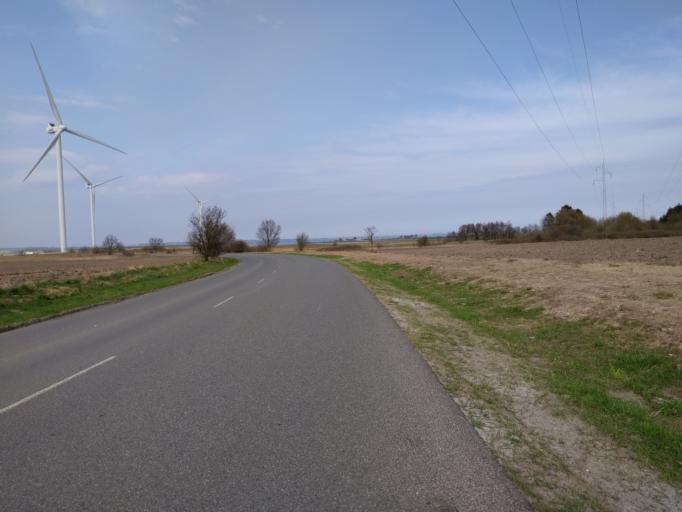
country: DK
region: South Denmark
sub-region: Kerteminde Kommune
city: Munkebo
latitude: 55.4679
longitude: 10.5522
